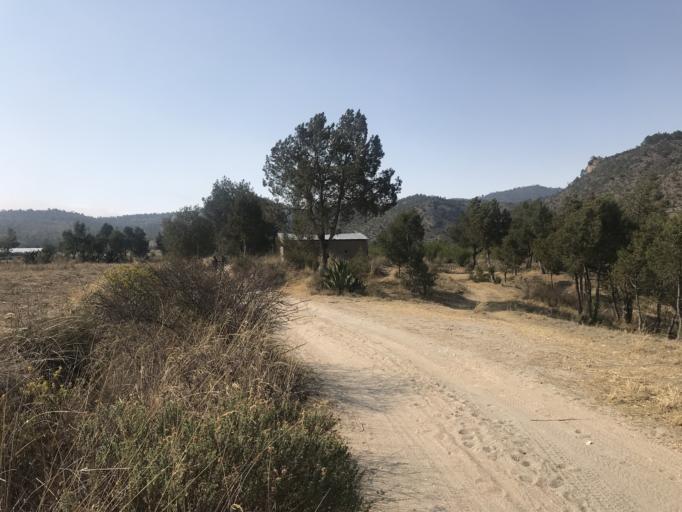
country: MX
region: Tlaxcala
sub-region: Emiliano Zapata
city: Emiliano Zapata
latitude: 19.6669
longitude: -97.8679
